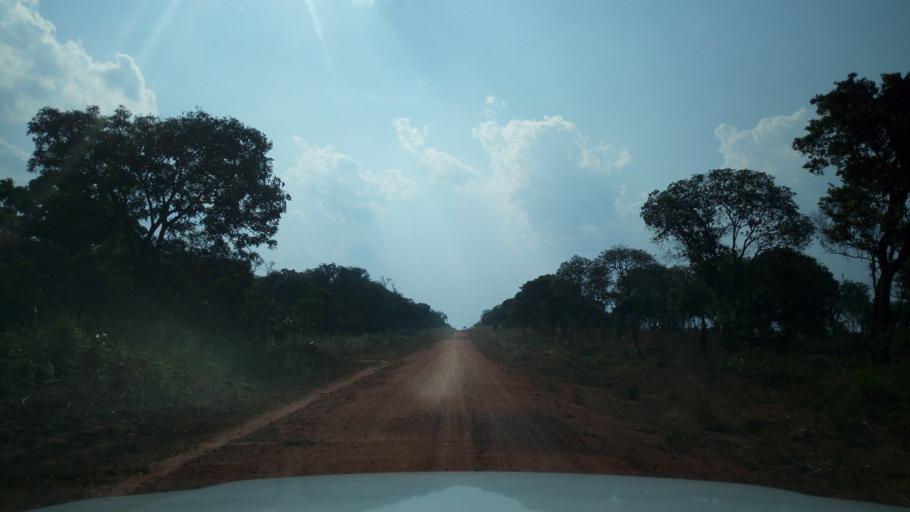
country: CD
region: Katanga
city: Kalemie
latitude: -5.2768
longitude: 28.8868
